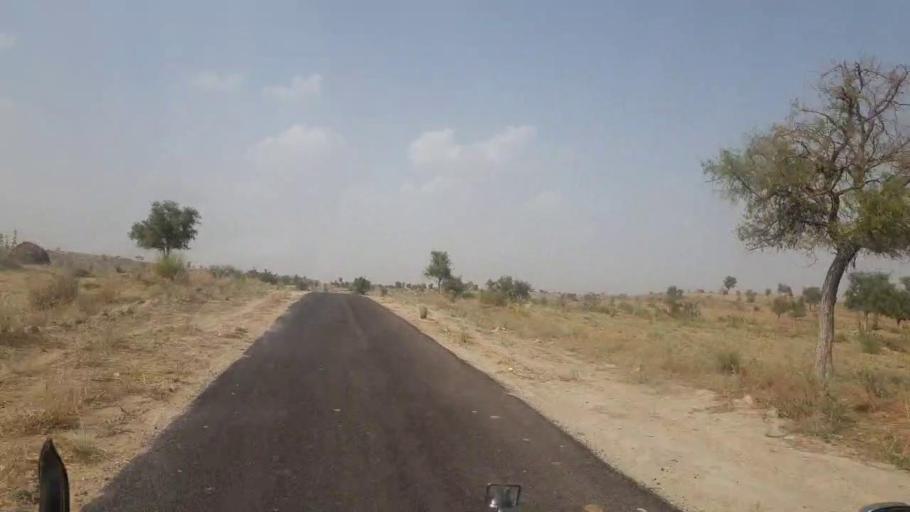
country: PK
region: Sindh
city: Islamkot
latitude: 25.1855
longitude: 70.2864
